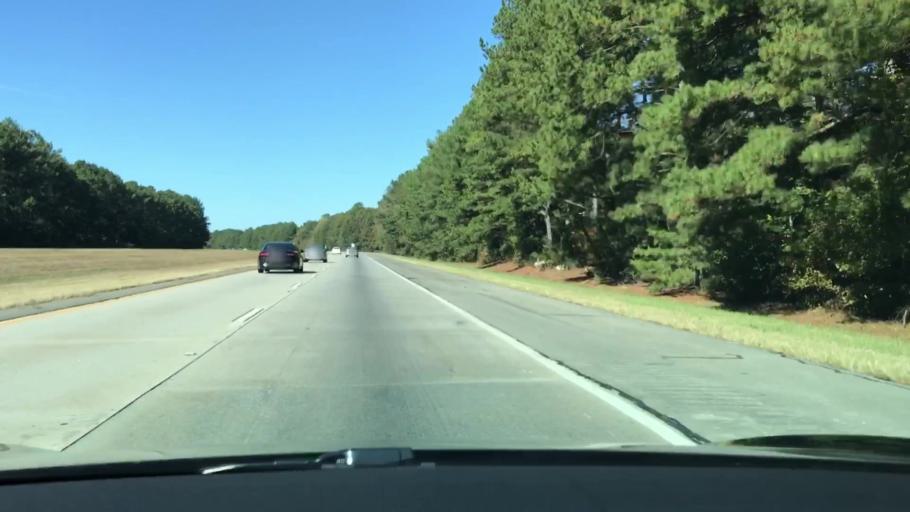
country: US
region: Georgia
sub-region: Taliaferro County
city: Crawfordville
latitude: 33.5358
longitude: -82.9940
